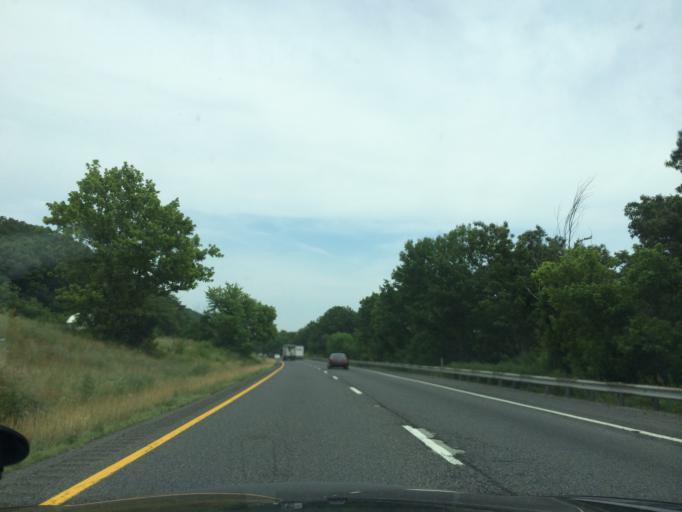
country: US
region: Maryland
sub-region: Washington County
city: Hancock
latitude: 39.6738
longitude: -78.0834
